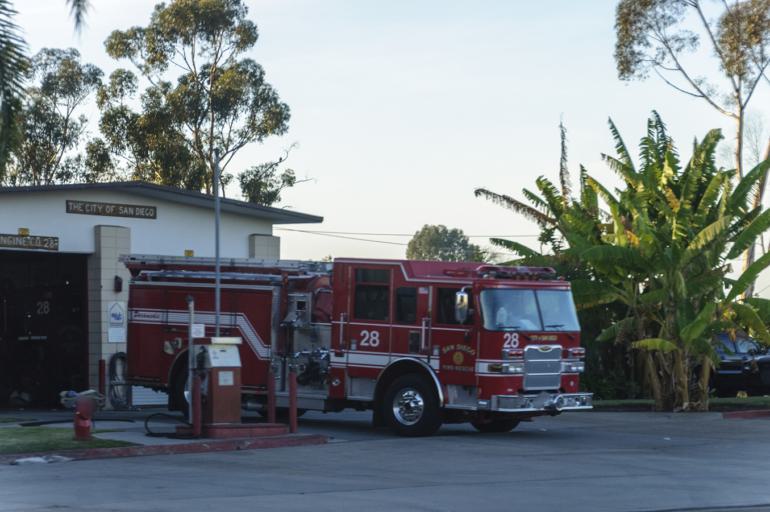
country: US
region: California
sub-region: San Diego County
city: San Diego
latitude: 32.8121
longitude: -117.1502
